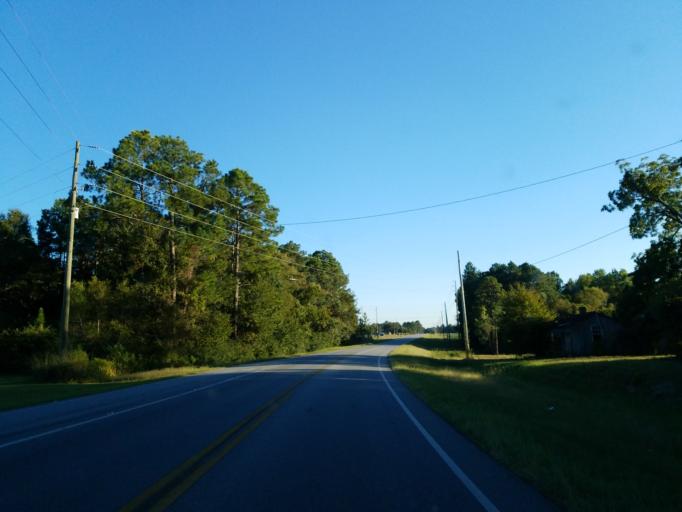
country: US
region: Georgia
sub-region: Worth County
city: Sylvester
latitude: 31.5530
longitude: -83.8431
